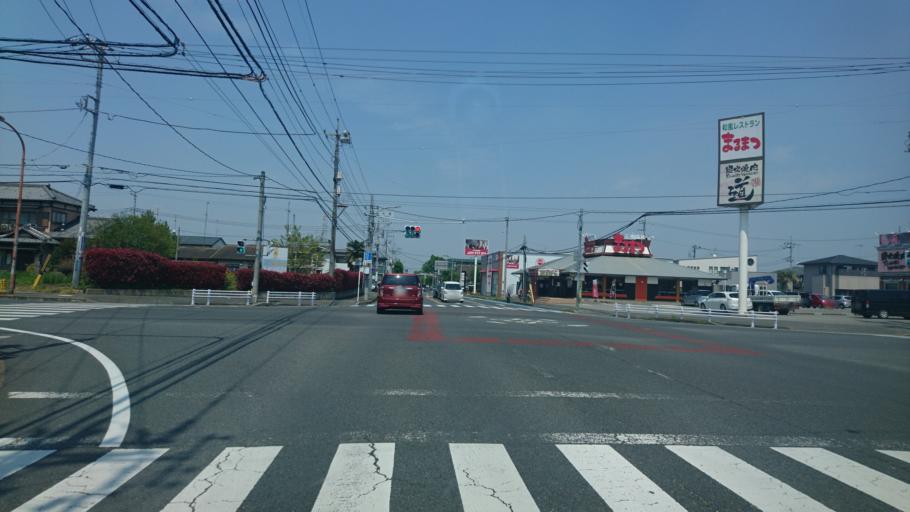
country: JP
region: Tochigi
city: Oyama
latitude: 36.3091
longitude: 139.8332
